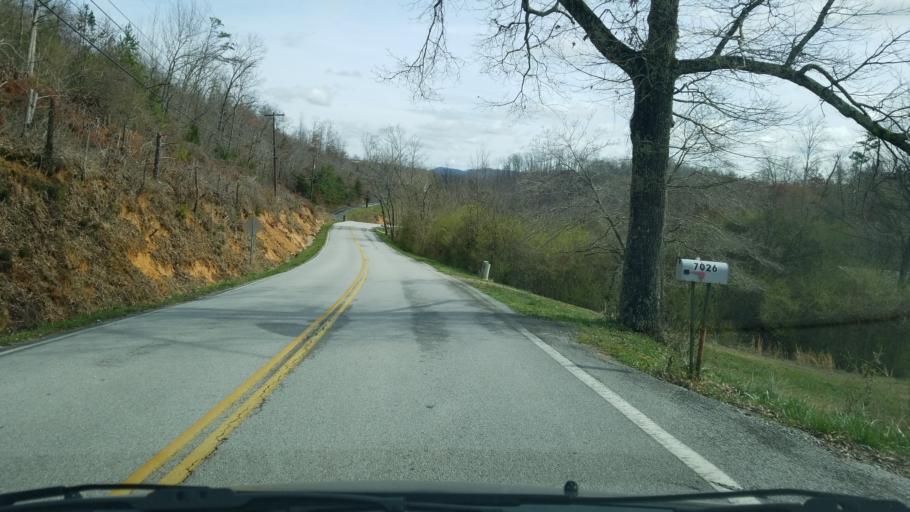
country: US
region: Tennessee
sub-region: Hamilton County
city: Harrison
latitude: 35.1397
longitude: -85.1051
